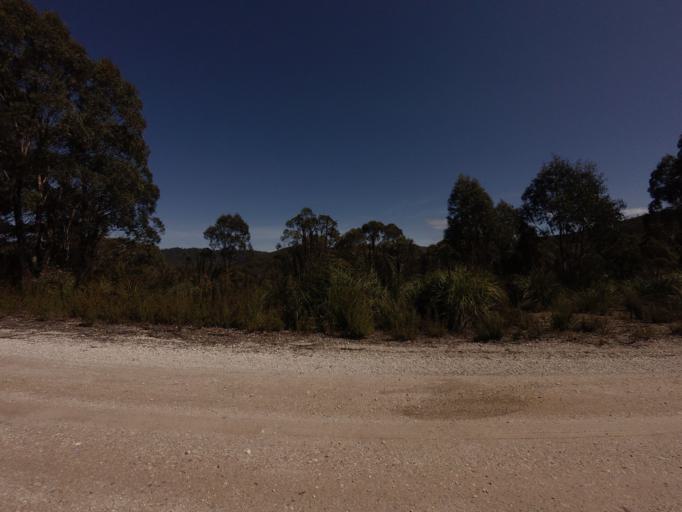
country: AU
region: Tasmania
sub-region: Huon Valley
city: Geeveston
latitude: -42.9103
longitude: 146.3628
